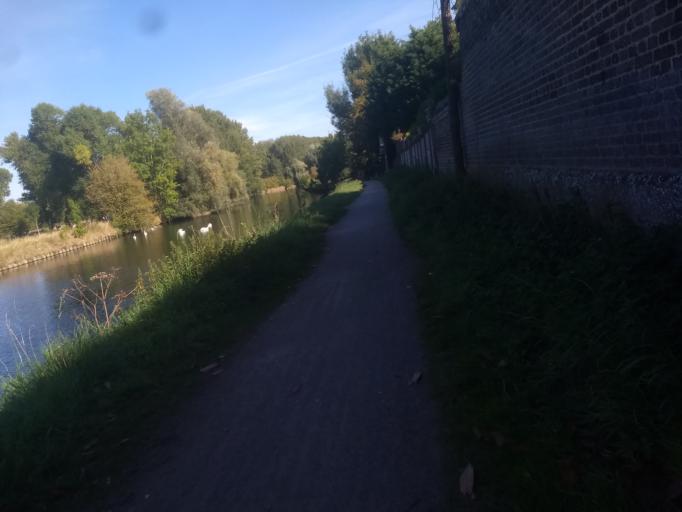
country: FR
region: Nord-Pas-de-Calais
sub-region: Departement du Pas-de-Calais
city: Feuchy
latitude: 50.2980
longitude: 2.8397
